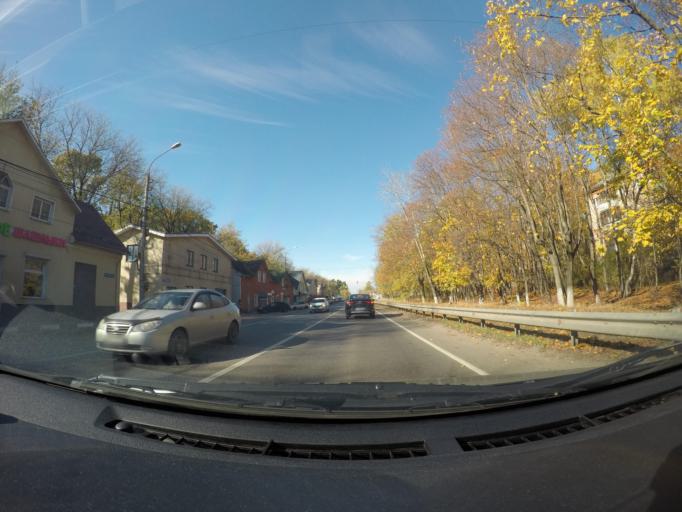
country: RU
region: Moskovskaya
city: Udel'naya
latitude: 55.6262
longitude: 38.0044
